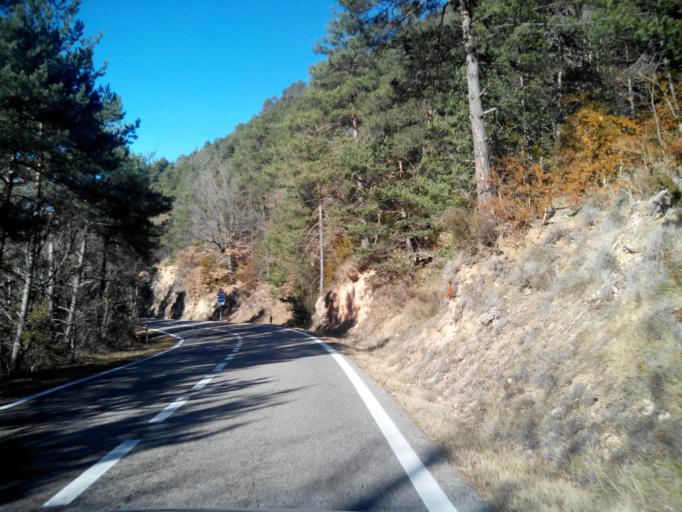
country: ES
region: Catalonia
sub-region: Provincia de Barcelona
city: Capolat
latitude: 42.0989
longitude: 1.7480
